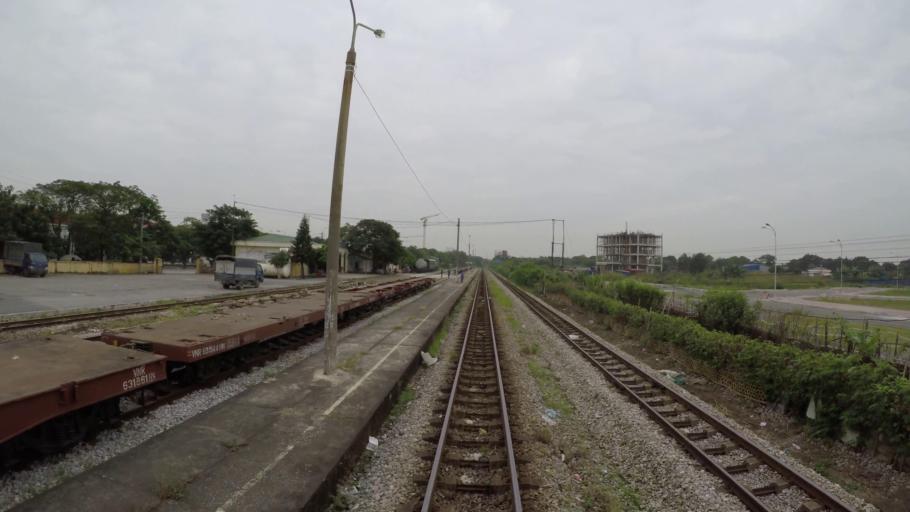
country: VN
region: Hai Phong
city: An Duong
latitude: 20.8836
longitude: 106.6103
